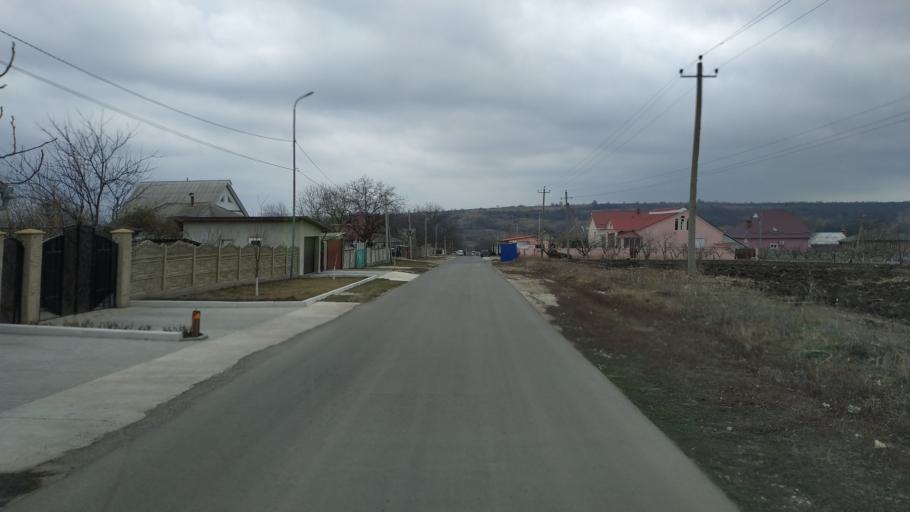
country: MD
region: Laloveni
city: Ialoveni
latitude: 46.9298
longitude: 28.7766
